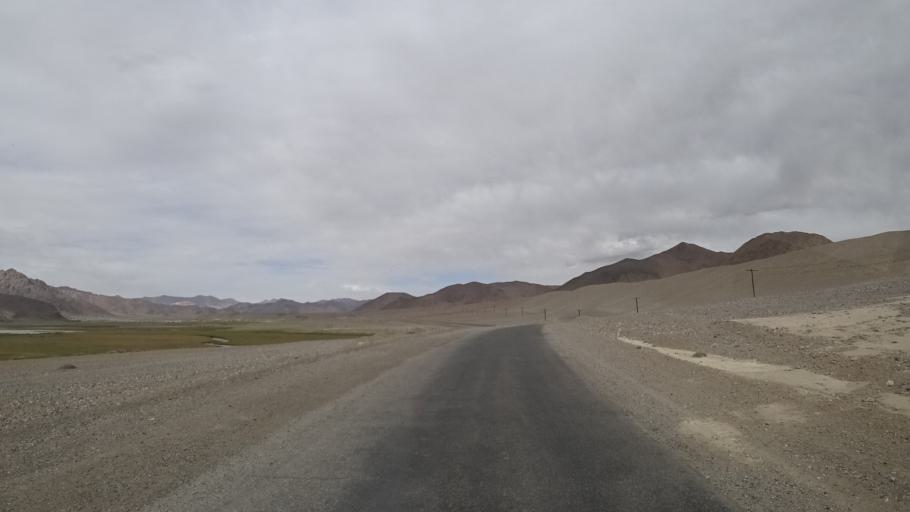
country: TJ
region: Gorno-Badakhshan
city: Murghob
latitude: 38.1262
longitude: 73.9439
